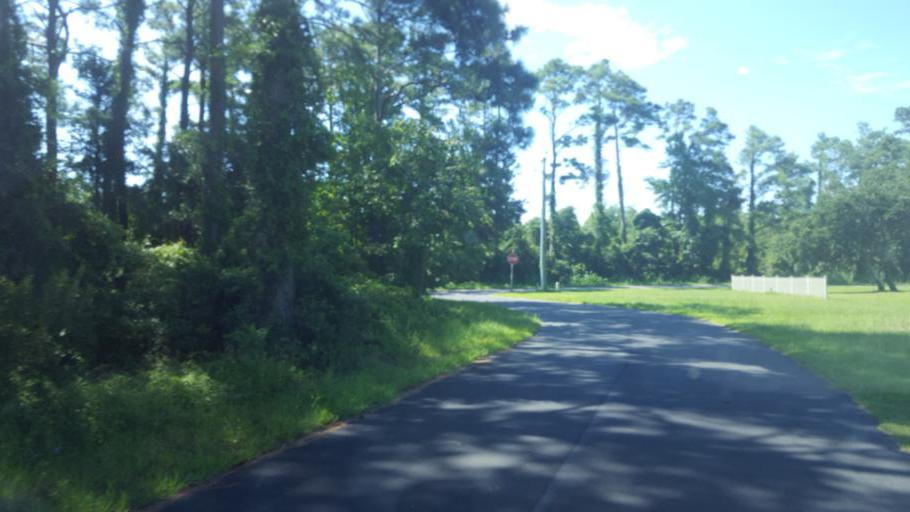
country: US
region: North Carolina
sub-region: Dare County
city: Kill Devil Hills
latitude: 36.0068
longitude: -75.6782
